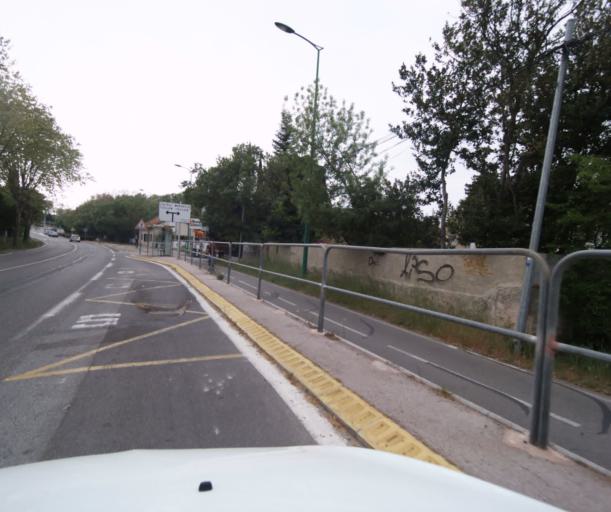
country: FR
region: Provence-Alpes-Cote d'Azur
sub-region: Departement du Var
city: La Garde
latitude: 43.1093
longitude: 6.0024
